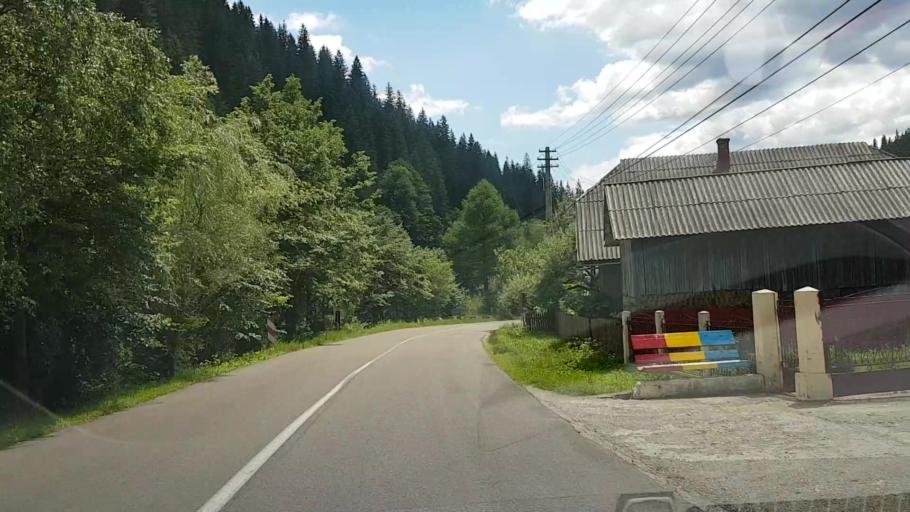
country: RO
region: Suceava
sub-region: Comuna Crucea
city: Crucea
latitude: 47.3428
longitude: 25.6103
